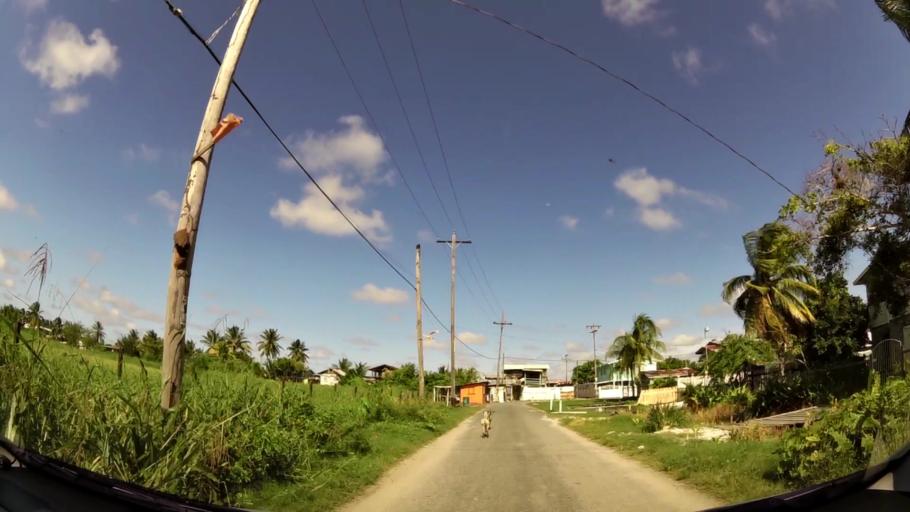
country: GY
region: Demerara-Mahaica
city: Georgetown
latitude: 6.8208
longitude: -58.1254
